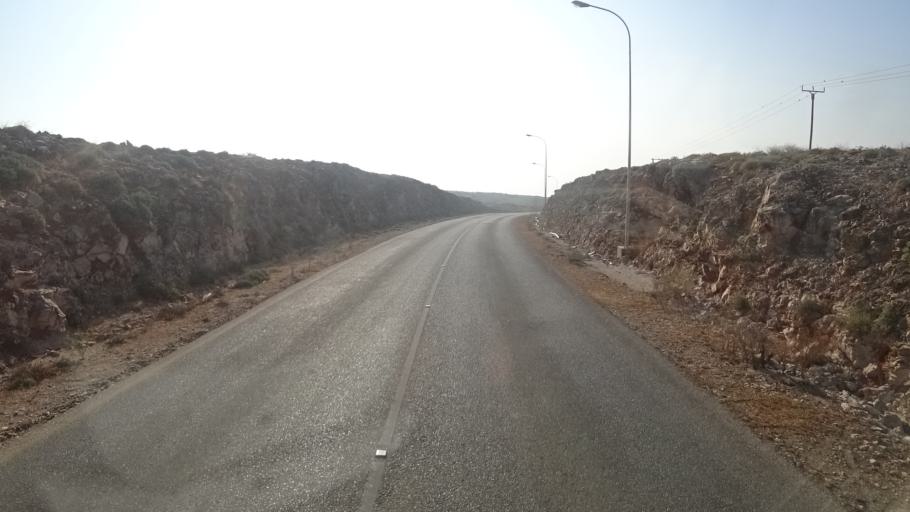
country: YE
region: Al Mahrah
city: Hawf
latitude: 16.7617
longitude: 53.2347
